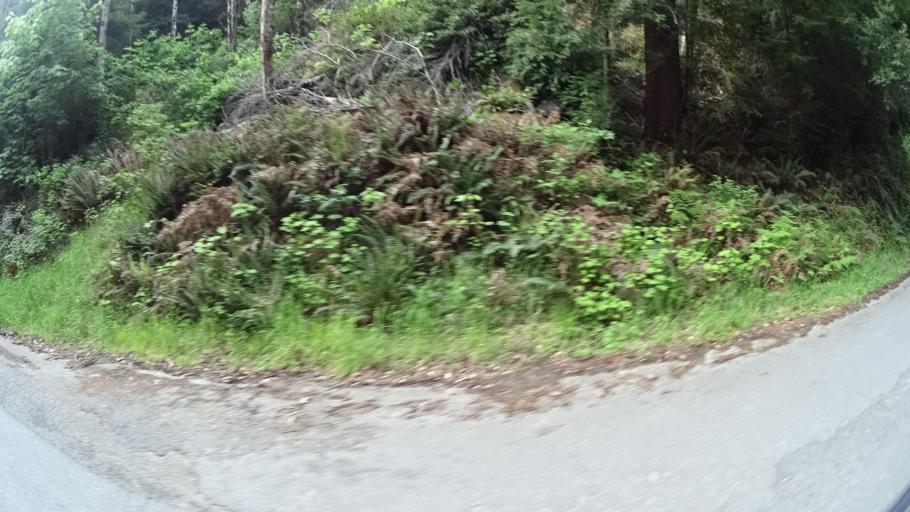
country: US
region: California
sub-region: Humboldt County
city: Redway
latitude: 40.3365
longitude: -123.9068
